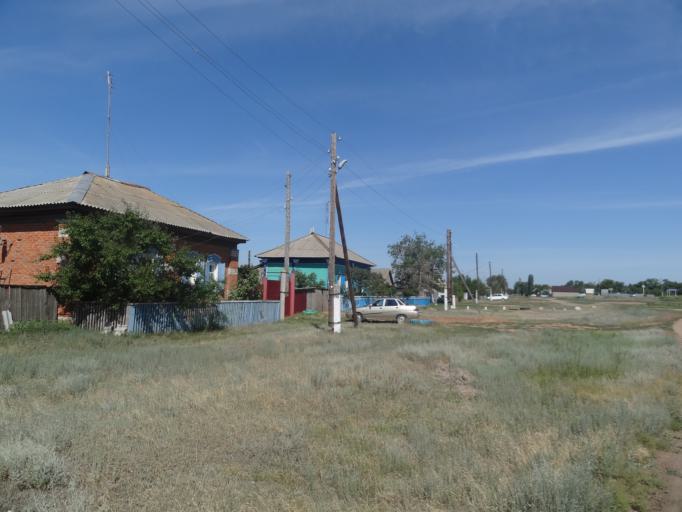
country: RU
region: Saratov
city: Krasnoarmeysk
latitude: 51.0832
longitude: 45.9587
